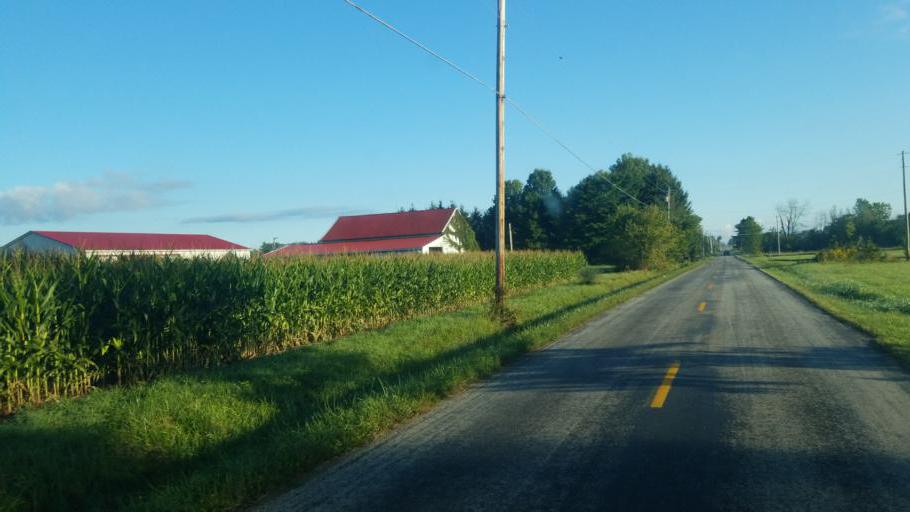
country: US
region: Ohio
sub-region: Lorain County
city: Wellington
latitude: 41.0393
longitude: -82.2595
